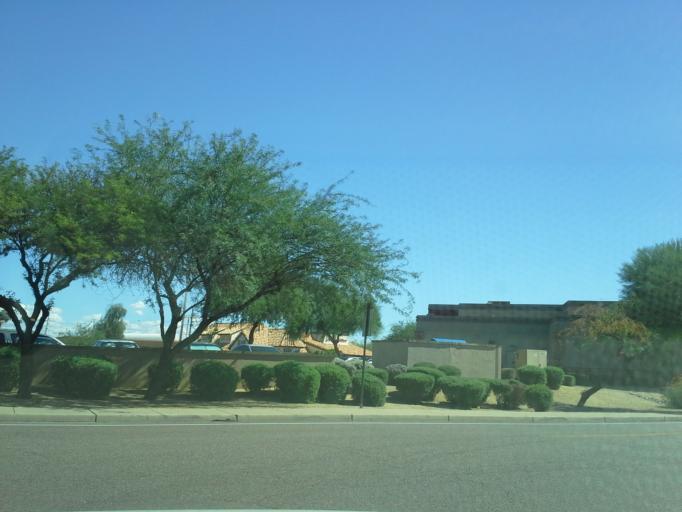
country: US
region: Arizona
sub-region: Maricopa County
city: Scottsdale
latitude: 33.5836
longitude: -111.8883
